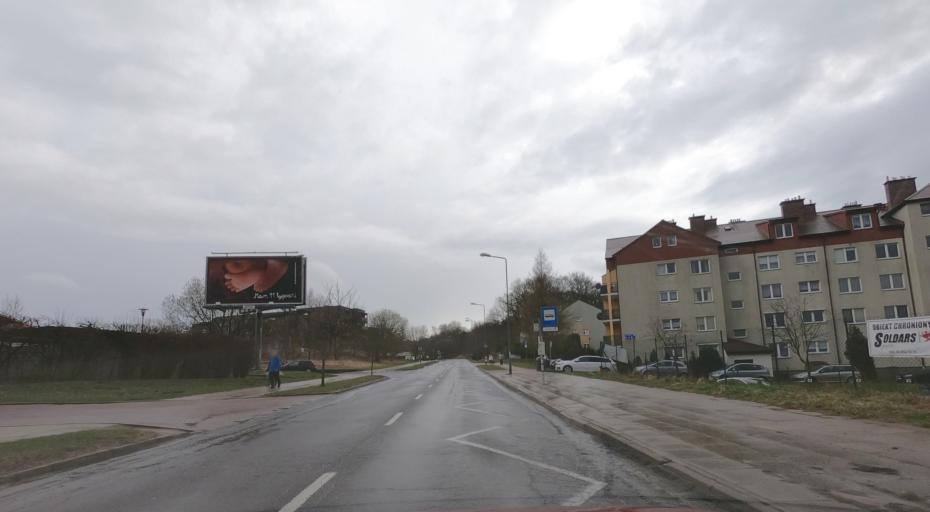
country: PL
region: West Pomeranian Voivodeship
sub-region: Szczecin
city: Szczecin
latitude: 53.3669
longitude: 14.6472
